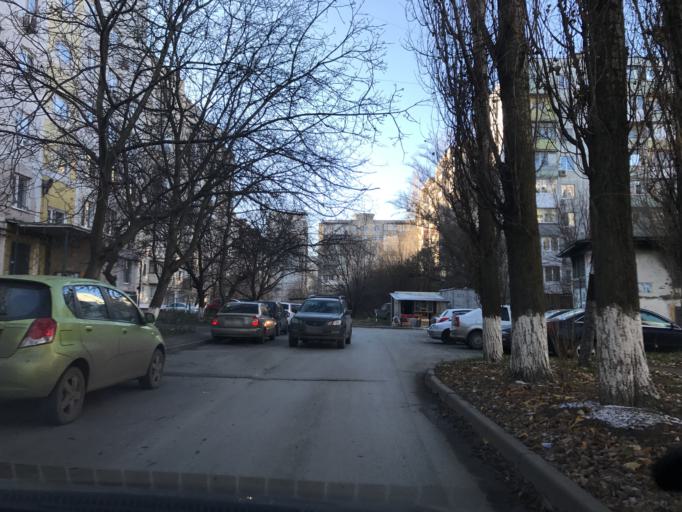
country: RU
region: Rostov
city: Rostov-na-Donu
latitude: 47.2130
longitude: 39.6252
